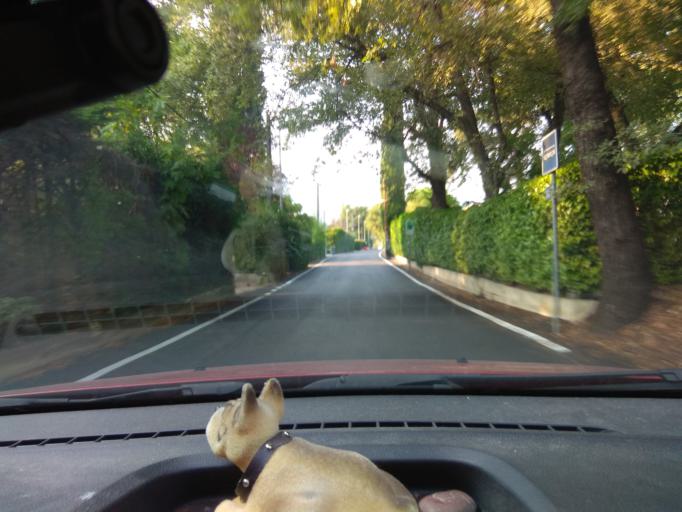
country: FR
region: Provence-Alpes-Cote d'Azur
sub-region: Departement des Alpes-Maritimes
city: Le Rouret
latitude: 43.6743
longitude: 7.0460
